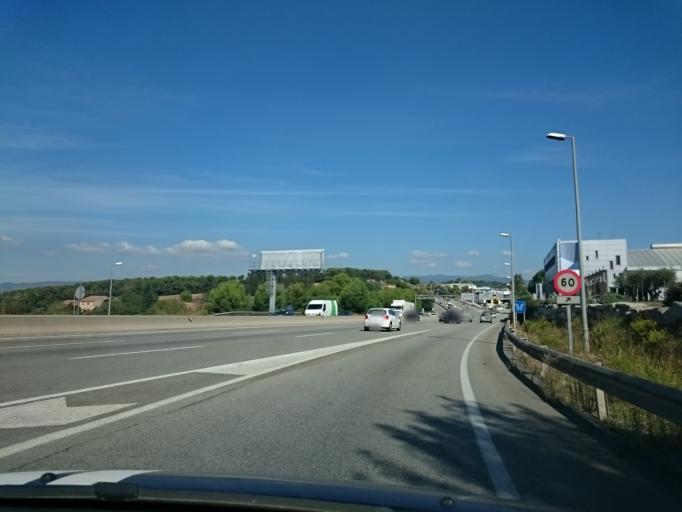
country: ES
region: Catalonia
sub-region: Provincia de Barcelona
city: Llica de Vall
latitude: 41.5883
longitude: 2.2592
